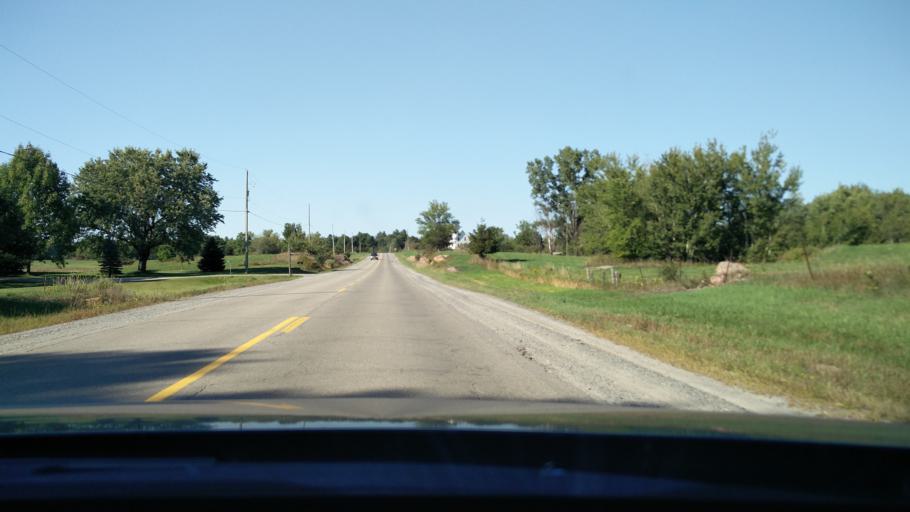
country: CA
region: Ontario
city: Perth
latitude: 44.6997
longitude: -76.4007
